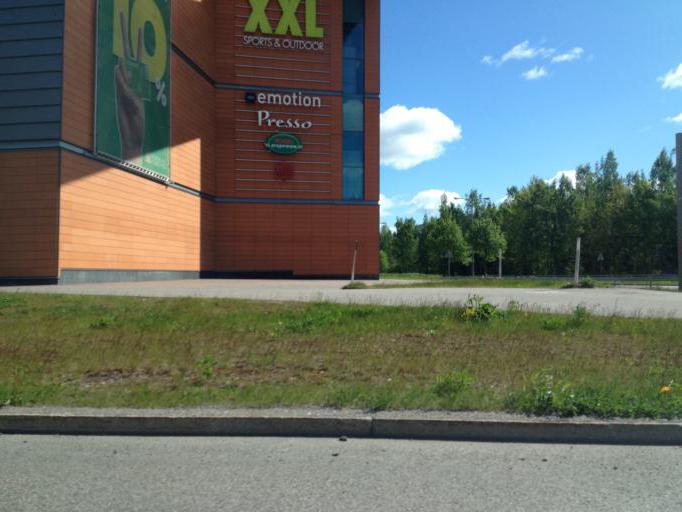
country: FI
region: Uusimaa
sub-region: Helsinki
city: Vantaa
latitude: 60.2127
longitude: 25.0873
